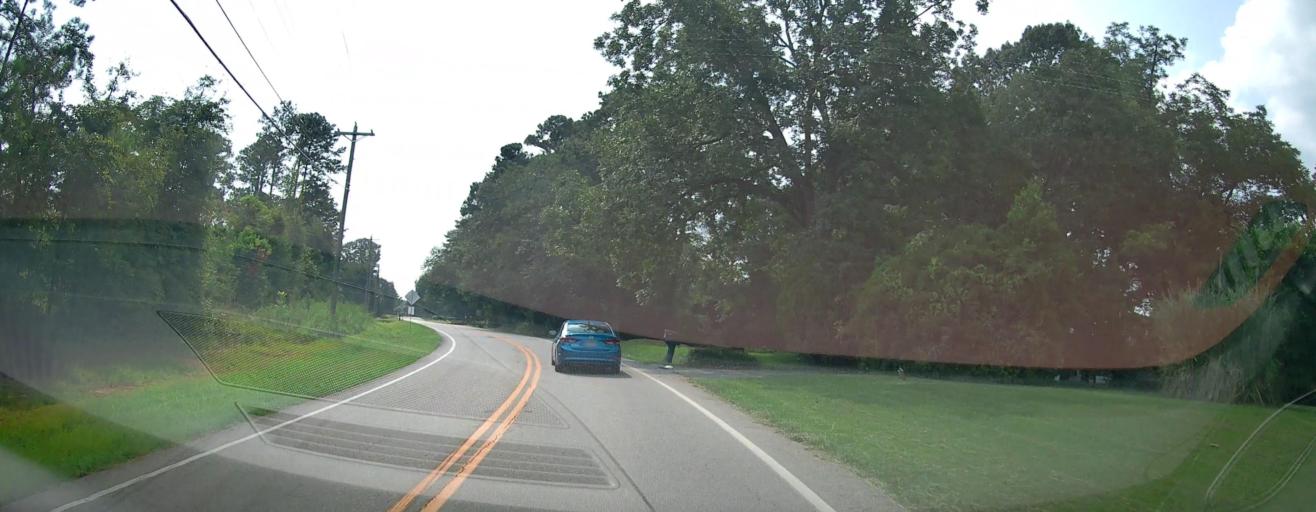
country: US
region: Georgia
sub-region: Houston County
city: Robins Air Force Base
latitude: 32.5765
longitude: -83.6112
